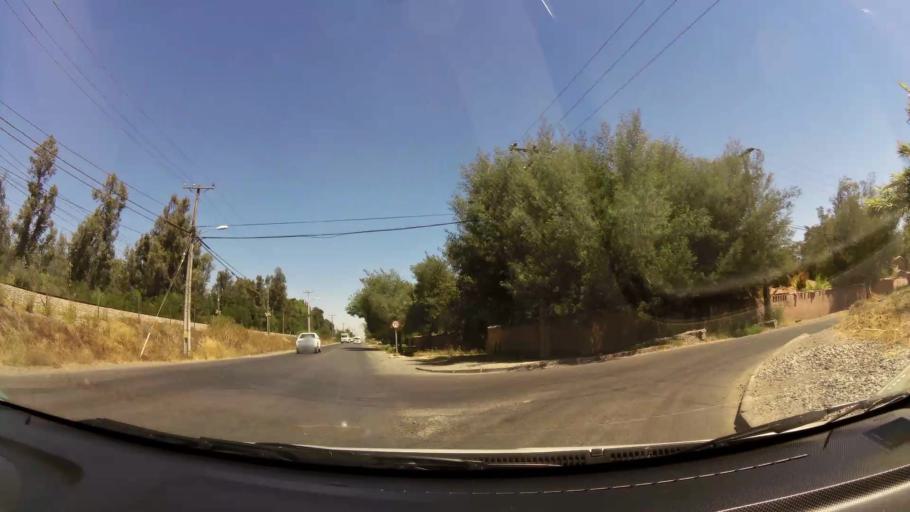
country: CL
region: O'Higgins
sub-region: Provincia de Cachapoal
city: Rancagua
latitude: -34.2348
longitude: -70.7888
